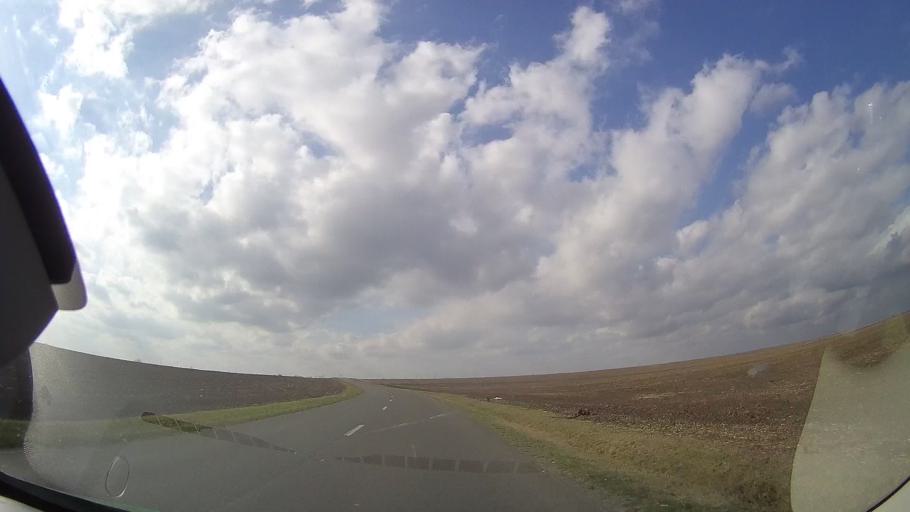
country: RO
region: Constanta
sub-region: Comuna Douazeci si Trei August
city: Dulcesti
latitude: 43.9136
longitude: 28.5601
